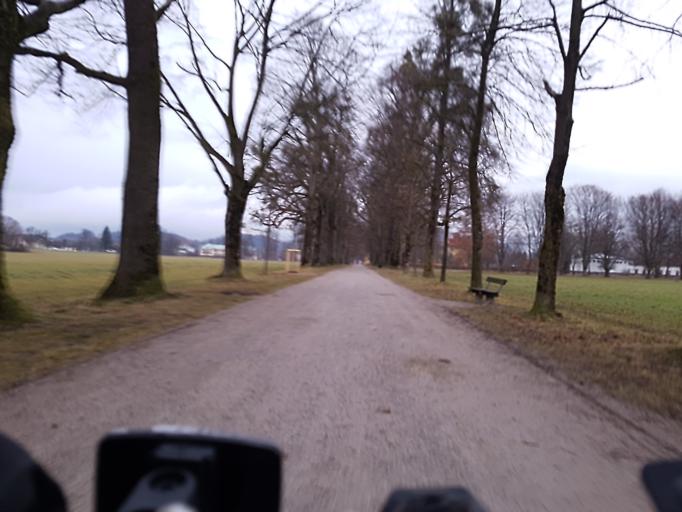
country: AT
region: Salzburg
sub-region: Politischer Bezirk Salzburg-Umgebung
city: Anif
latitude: 47.7746
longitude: 13.0612
